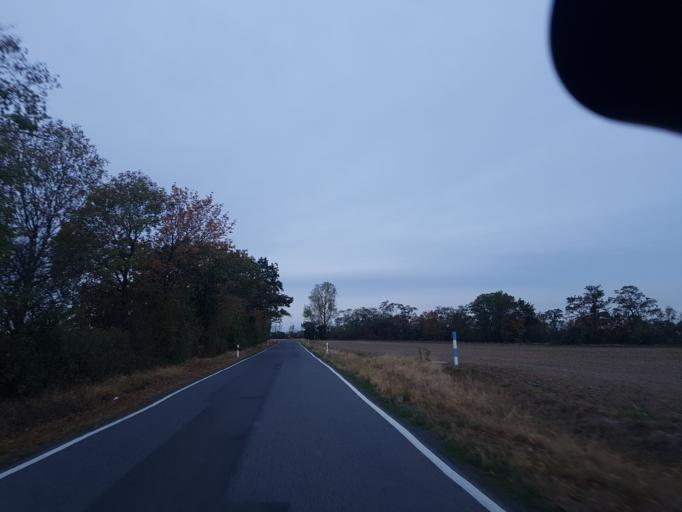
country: DE
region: Brandenburg
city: Muhlberg
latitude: 51.4993
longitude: 13.2444
